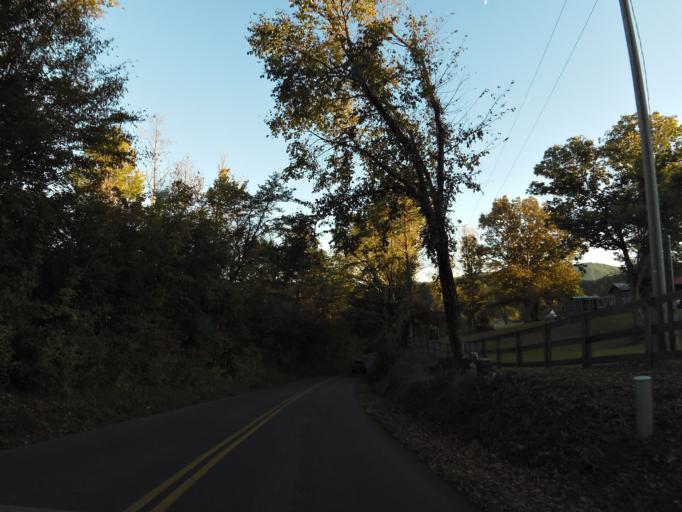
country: US
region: Tennessee
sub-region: Sevier County
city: Seymour
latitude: 35.8090
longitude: -83.7547
